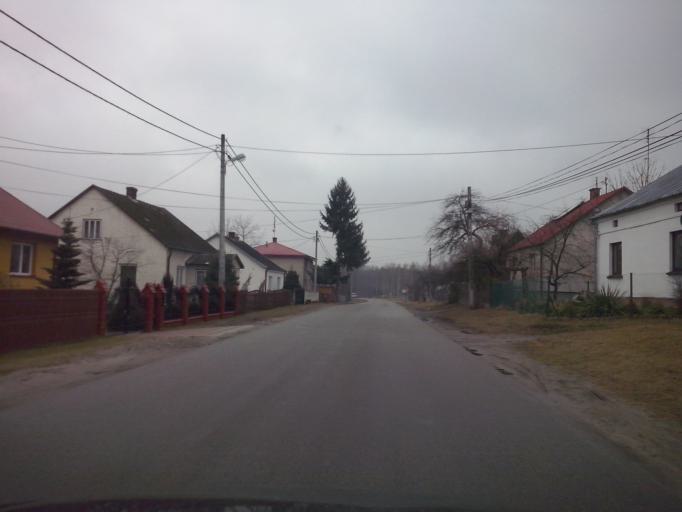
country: PL
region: Subcarpathian Voivodeship
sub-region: Powiat nizanski
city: Bieliny
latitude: 50.4255
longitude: 22.3184
